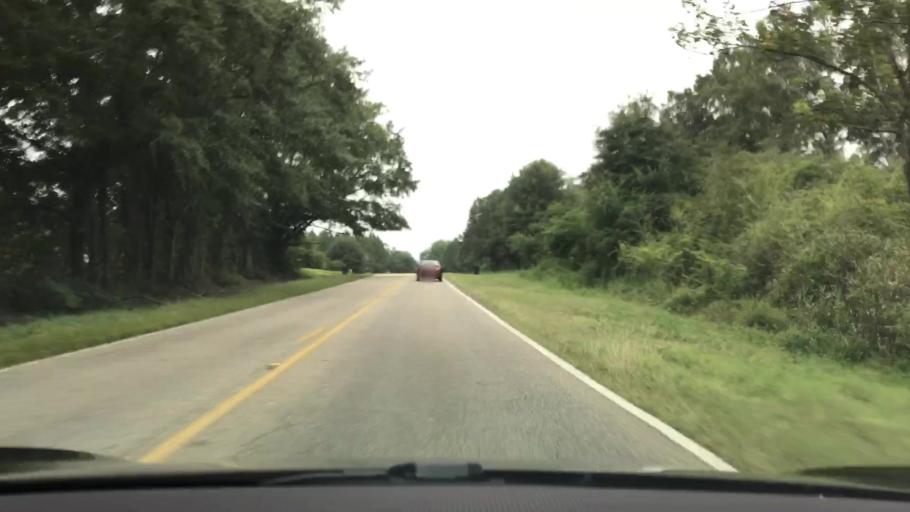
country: US
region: Alabama
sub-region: Geneva County
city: Samson
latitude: 31.1895
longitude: -86.1537
